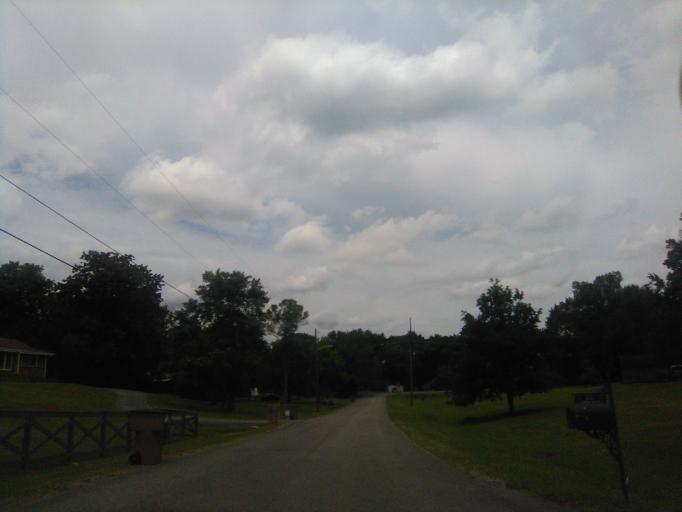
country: US
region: Tennessee
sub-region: Davidson County
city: Belle Meade
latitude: 36.1164
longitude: -86.8901
